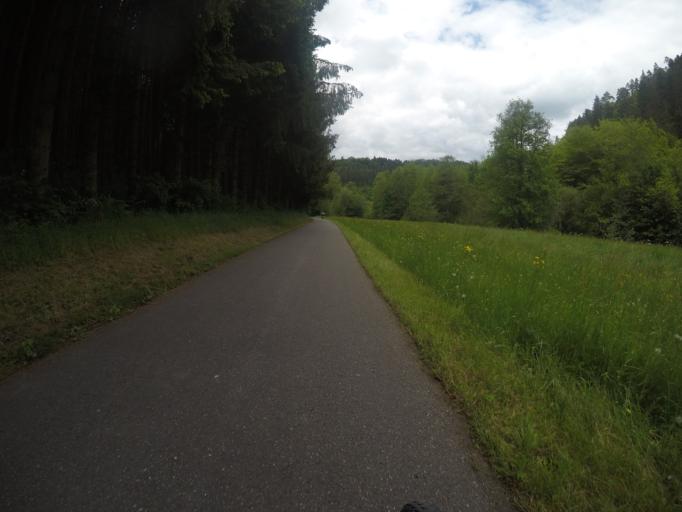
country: DE
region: Baden-Wuerttemberg
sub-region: Karlsruhe Region
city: Neubulach
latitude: 48.6512
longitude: 8.7262
